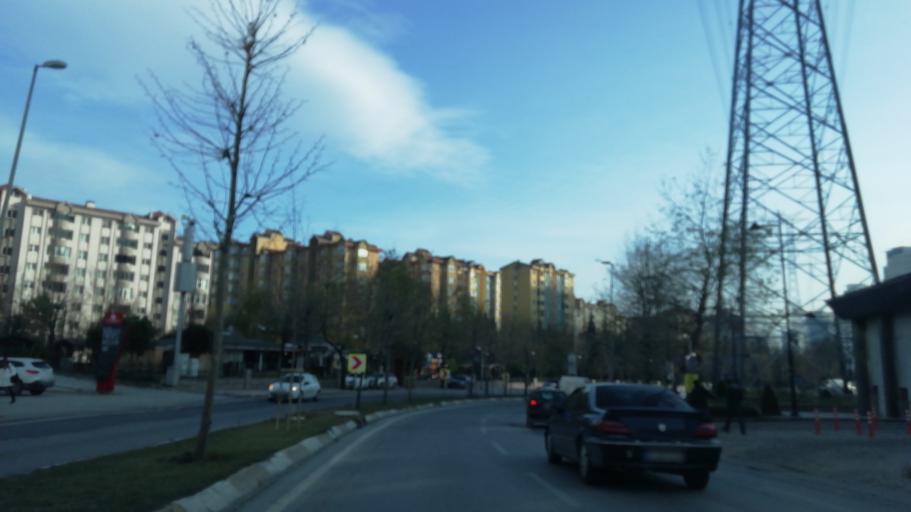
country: TR
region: Istanbul
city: Esenyurt
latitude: 41.0631
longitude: 28.6683
